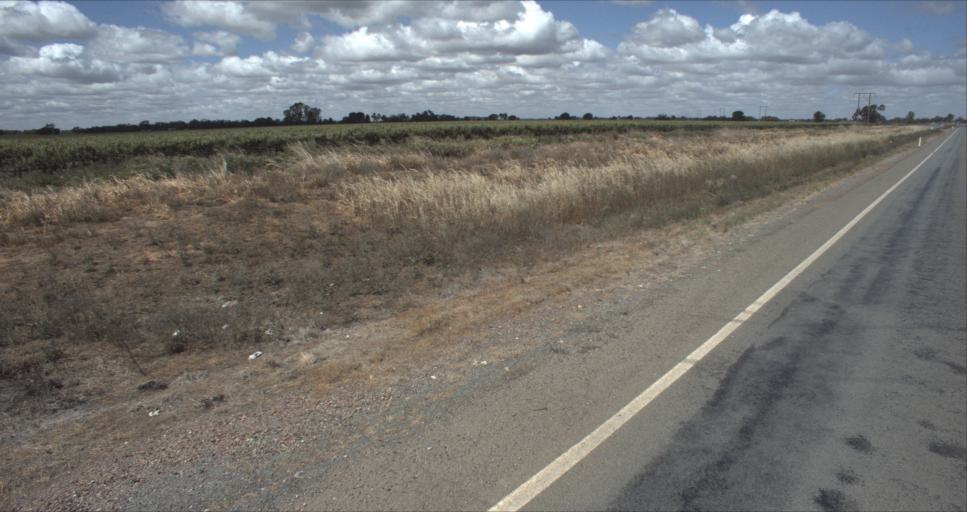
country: AU
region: New South Wales
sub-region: Murrumbidgee Shire
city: Darlington Point
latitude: -34.5043
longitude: 146.1875
